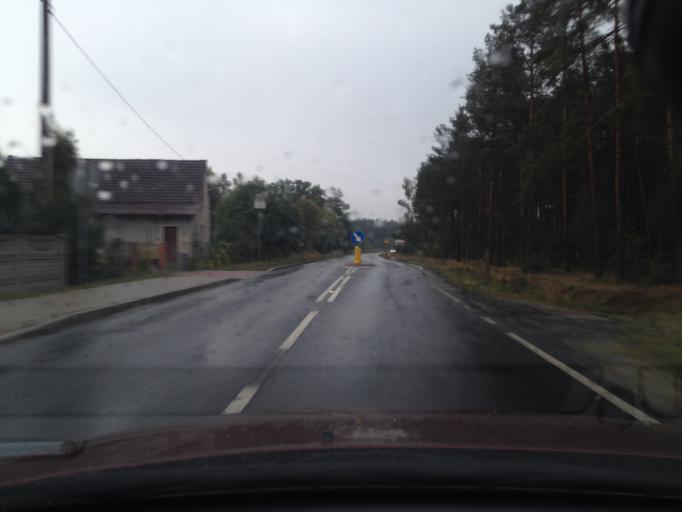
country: PL
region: Lubusz
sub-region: Powiat zaganski
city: Ilowa
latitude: 51.4672
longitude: 15.1998
